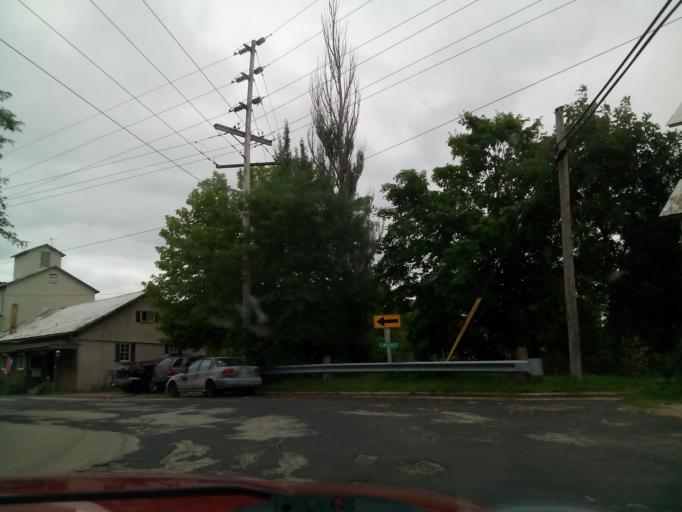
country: US
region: Wisconsin
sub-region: Outagamie County
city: Hortonville
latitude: 44.3312
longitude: -88.6412
